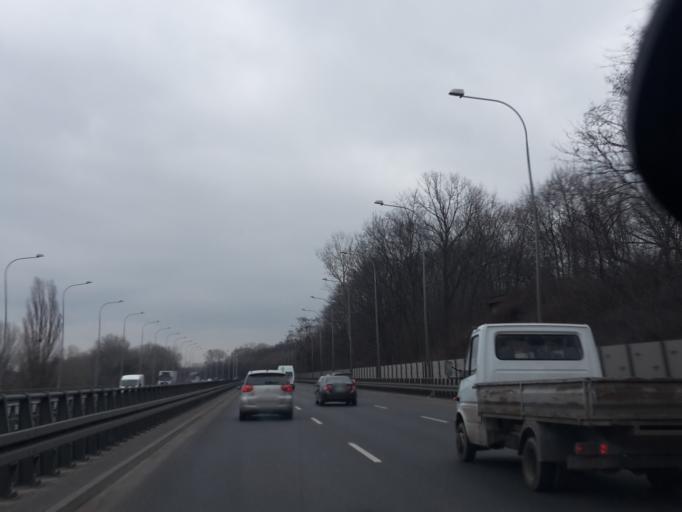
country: PL
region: Masovian Voivodeship
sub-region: Warszawa
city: Bielany
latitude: 52.2983
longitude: 20.9596
